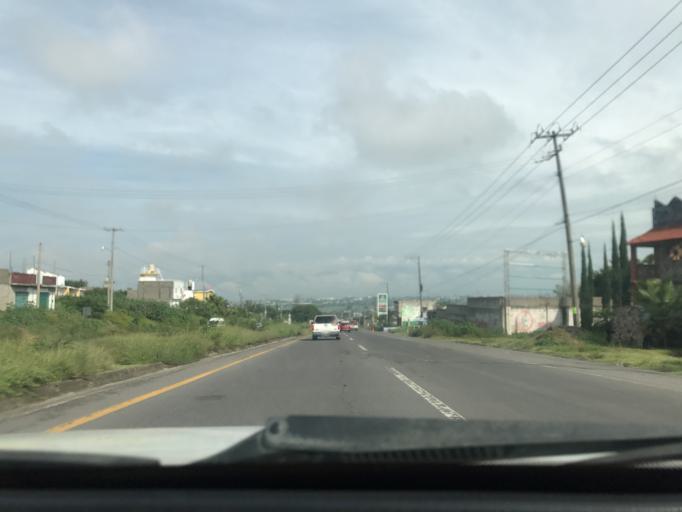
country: MX
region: Morelos
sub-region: Yecapixtla
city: Juan Morales
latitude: 18.8180
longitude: -98.9186
